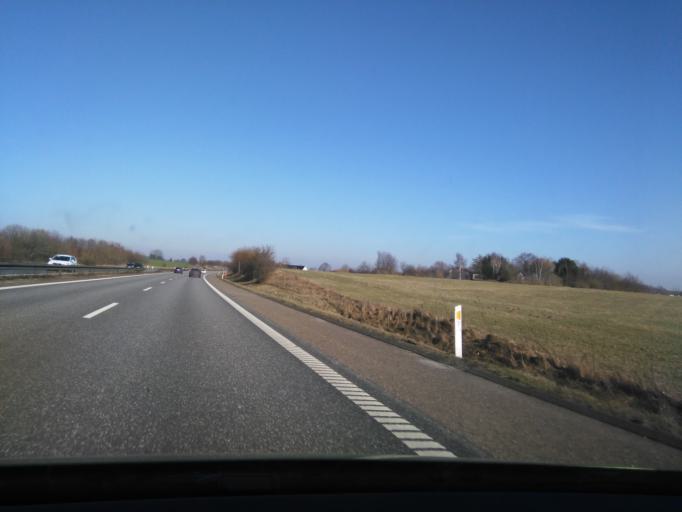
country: DK
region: Zealand
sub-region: Soro Kommune
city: Soro
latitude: 55.4517
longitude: 11.5287
